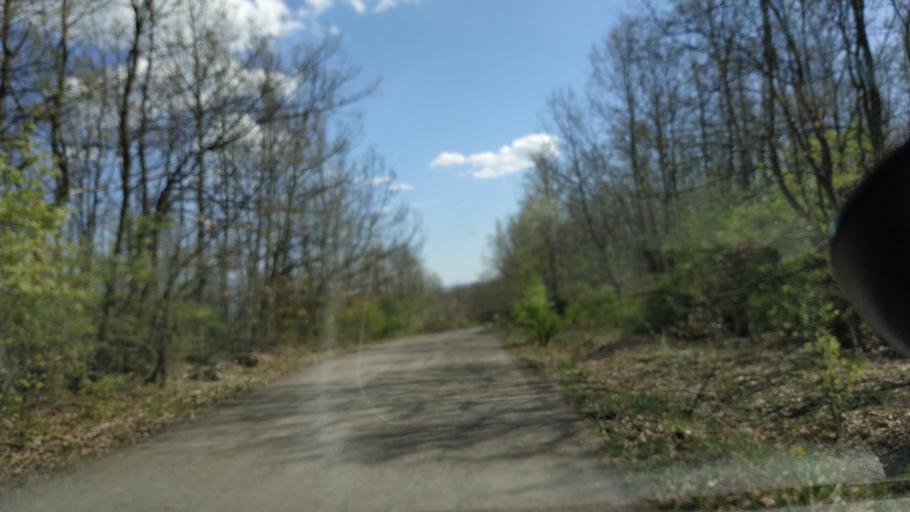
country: RS
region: Central Serbia
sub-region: Zajecarski Okrug
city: Soko Banja
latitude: 43.5412
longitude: 21.9034
